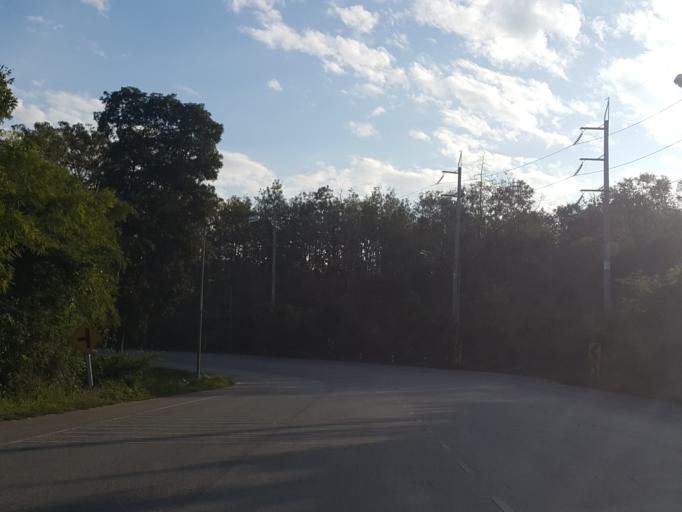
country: TH
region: Lampang
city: Chae Hom
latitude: 18.5442
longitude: 99.5672
